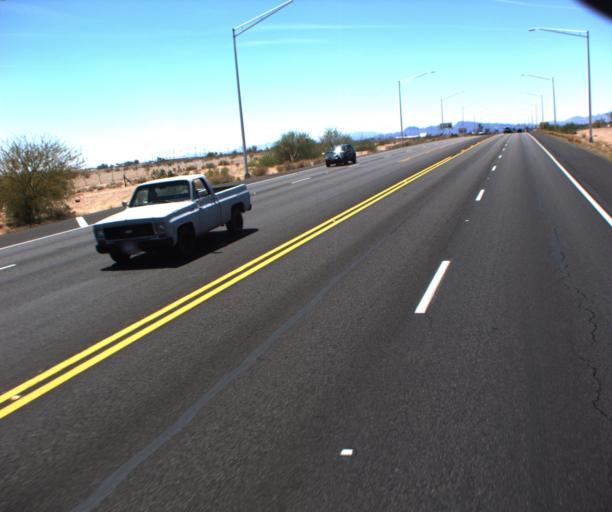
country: US
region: Arizona
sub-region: La Paz County
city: Parker
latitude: 34.1597
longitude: -114.2674
